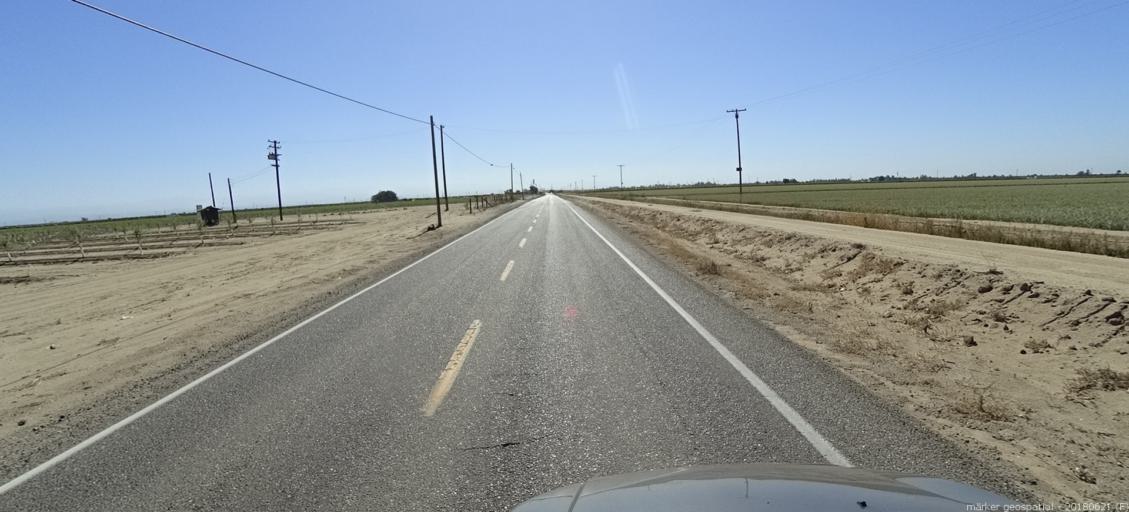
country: US
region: California
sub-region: Fresno County
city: Biola
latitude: 36.8512
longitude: -119.9621
